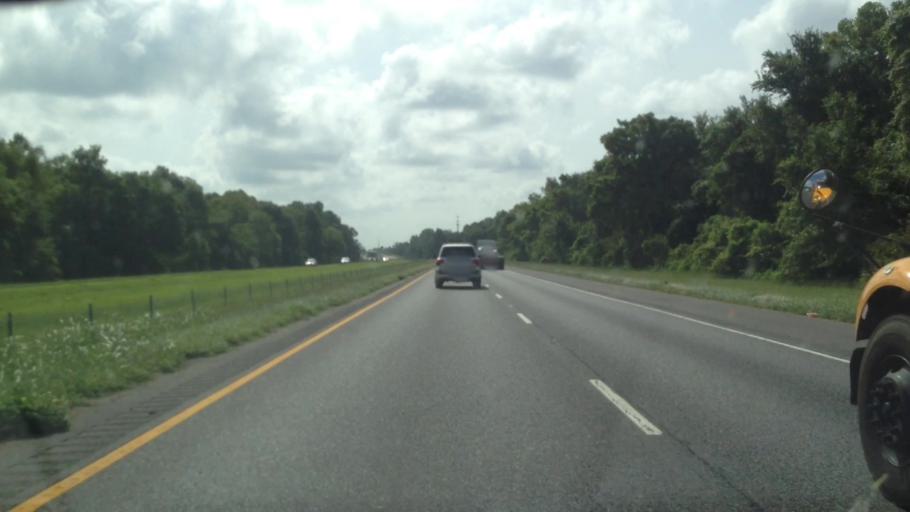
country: US
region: Louisiana
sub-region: Ascension Parish
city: Sorrento
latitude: 30.1566
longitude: -90.8229
